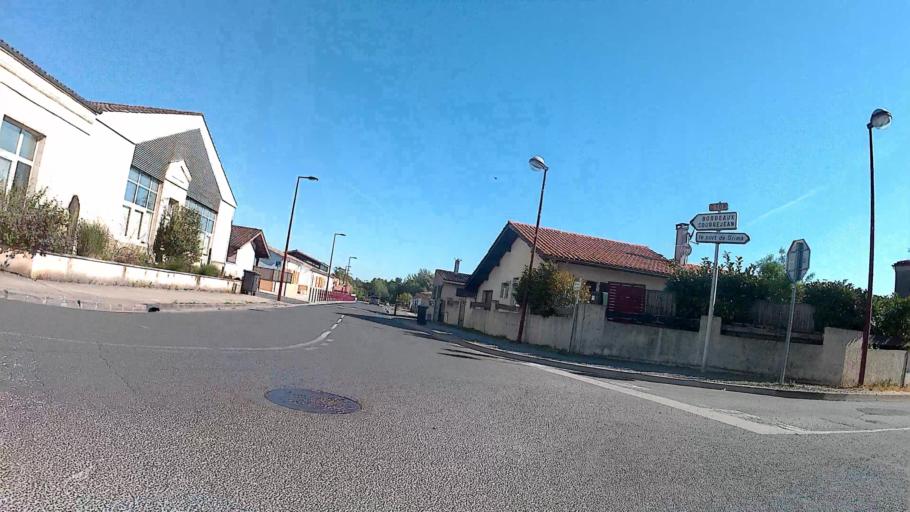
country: FR
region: Aquitaine
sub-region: Departement de la Gironde
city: Cadaujac
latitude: 44.7554
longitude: -0.5293
